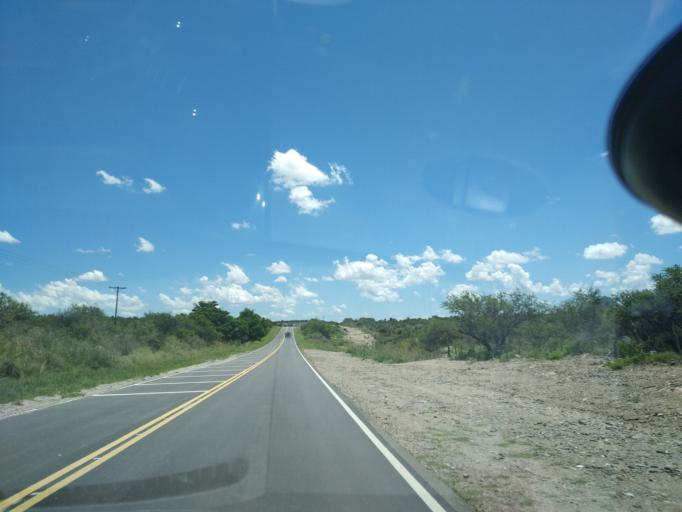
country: AR
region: Cordoba
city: Salsacate
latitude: -31.3481
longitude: -65.0819
